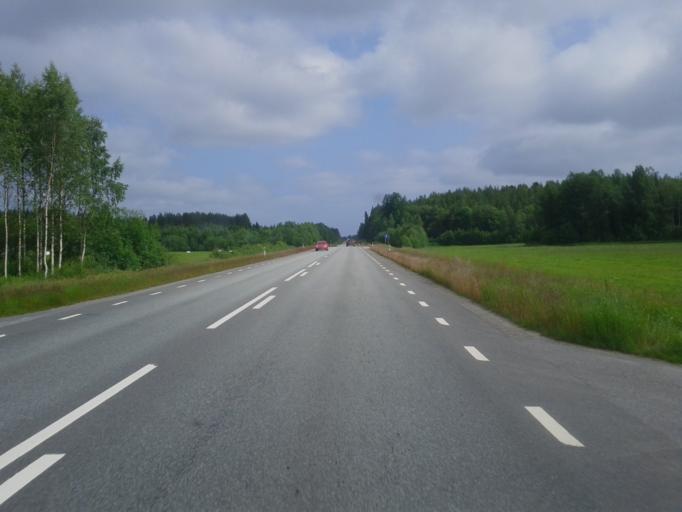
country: SE
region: Vaesterbotten
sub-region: Skelleftea Kommun
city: Burea
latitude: 64.3373
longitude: 21.2727
